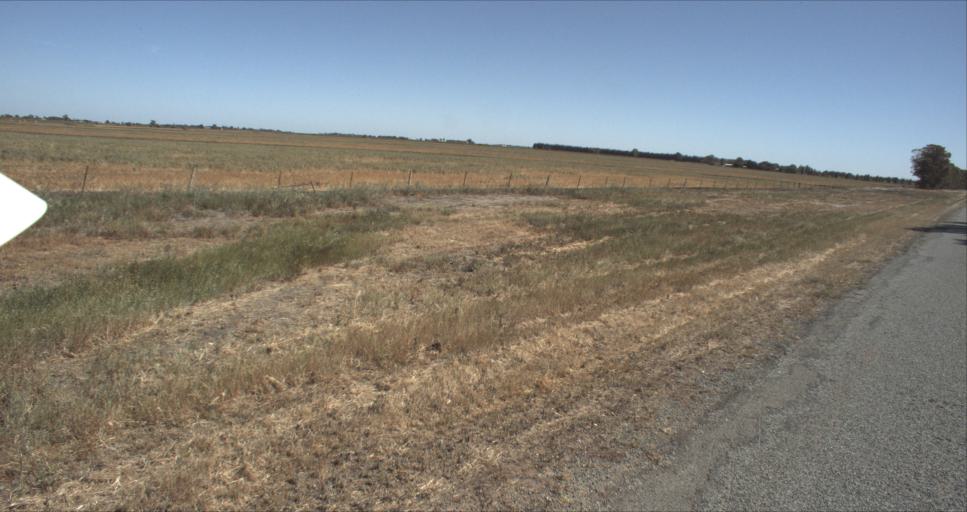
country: AU
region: New South Wales
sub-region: Leeton
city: Leeton
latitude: -34.5394
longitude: 146.3168
